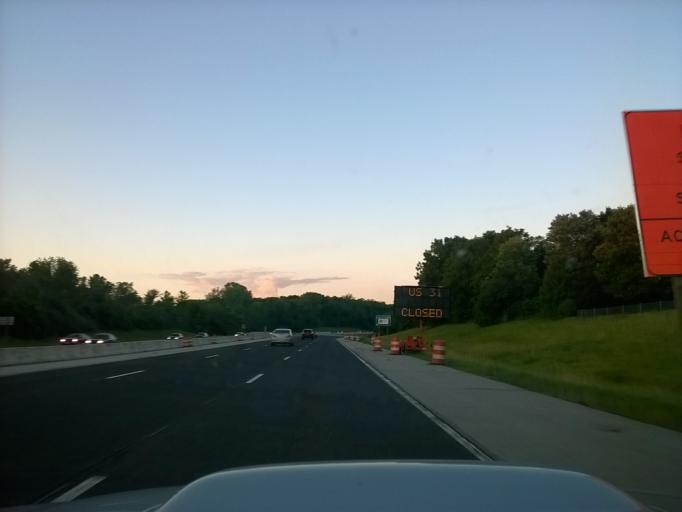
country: US
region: Indiana
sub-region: Marion County
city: Meridian Hills
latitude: 39.9272
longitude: -86.1779
